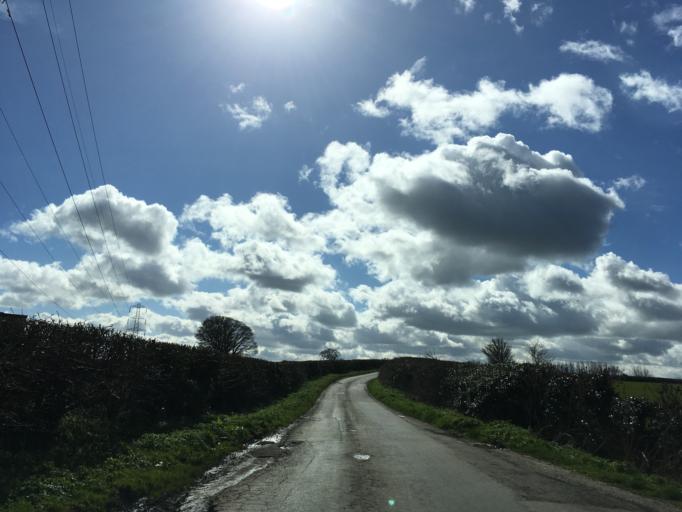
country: GB
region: England
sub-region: South Gloucestershire
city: Horton
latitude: 51.5492
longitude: -2.3409
